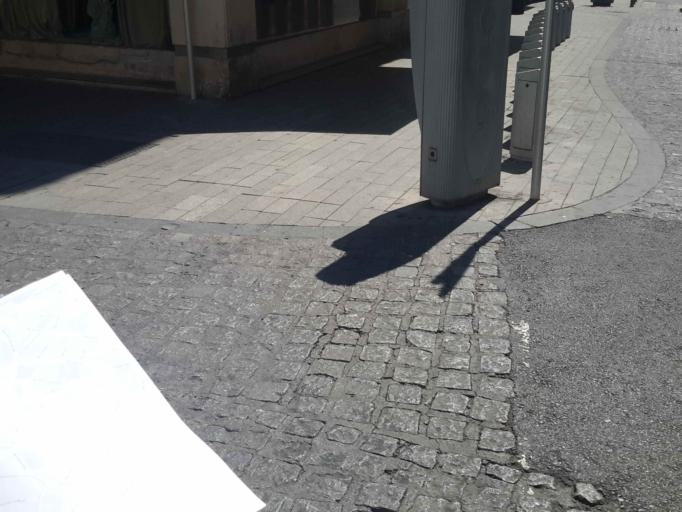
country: ES
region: Andalusia
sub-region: Provincia de Sevilla
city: Sevilla
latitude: 37.3897
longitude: -5.9913
